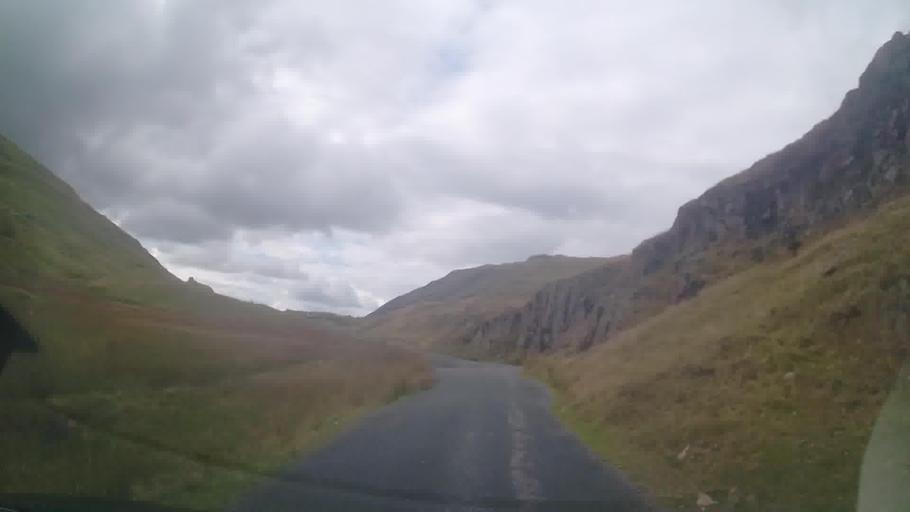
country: GB
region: England
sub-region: Cumbria
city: Ambleside
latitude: 54.4152
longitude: -3.1133
